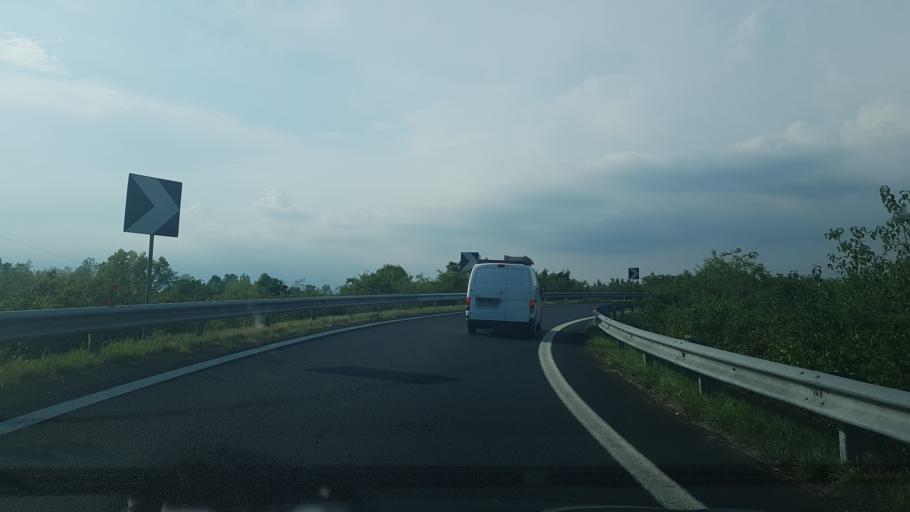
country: IT
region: Friuli Venezia Giulia
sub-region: Provincia di Udine
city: Zugliano-Terenzano-Cargnacco
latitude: 46.0142
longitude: 13.2240
